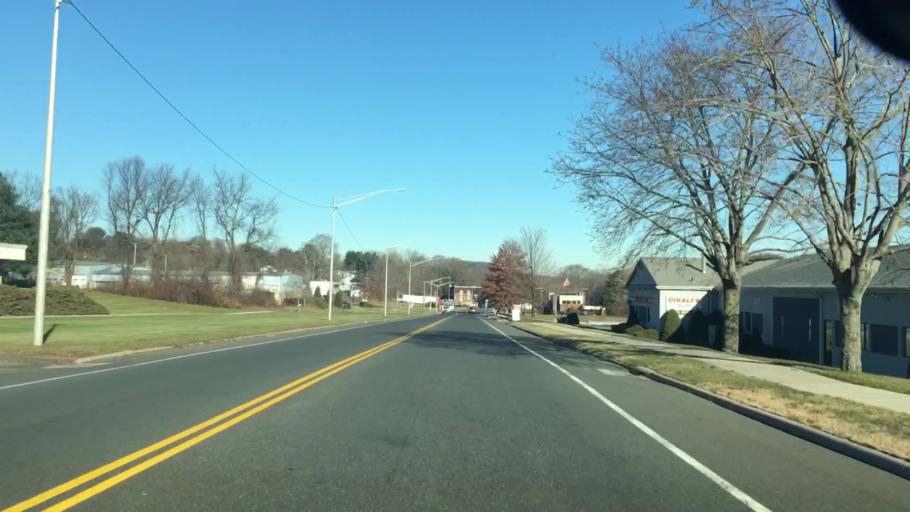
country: US
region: Connecticut
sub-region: New Haven County
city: Meriden
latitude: 41.5224
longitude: -72.7600
